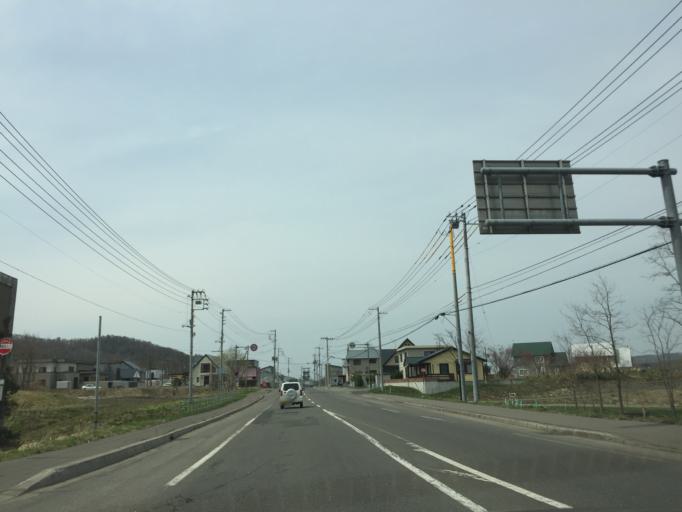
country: JP
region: Hokkaido
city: Akabira
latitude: 43.5416
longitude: 142.0679
